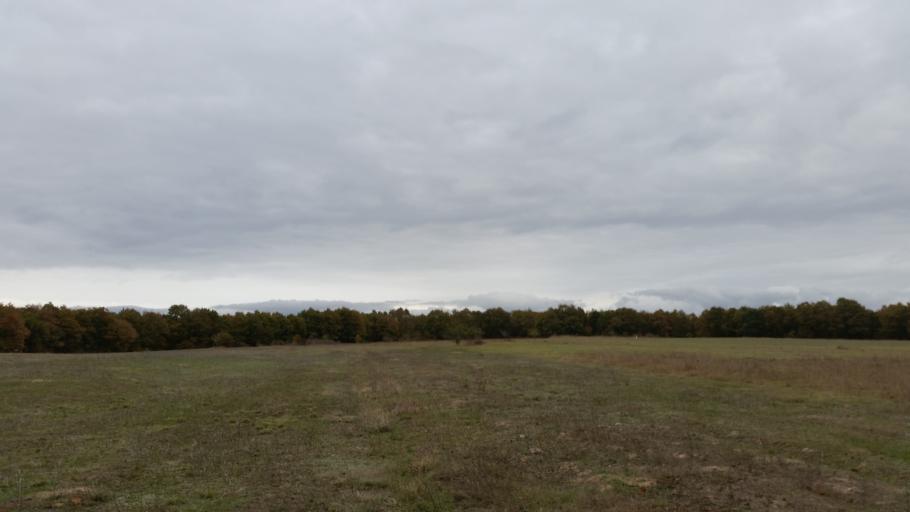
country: TR
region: Tekirdag
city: Cerkezkoey
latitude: 41.3838
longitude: 28.0100
